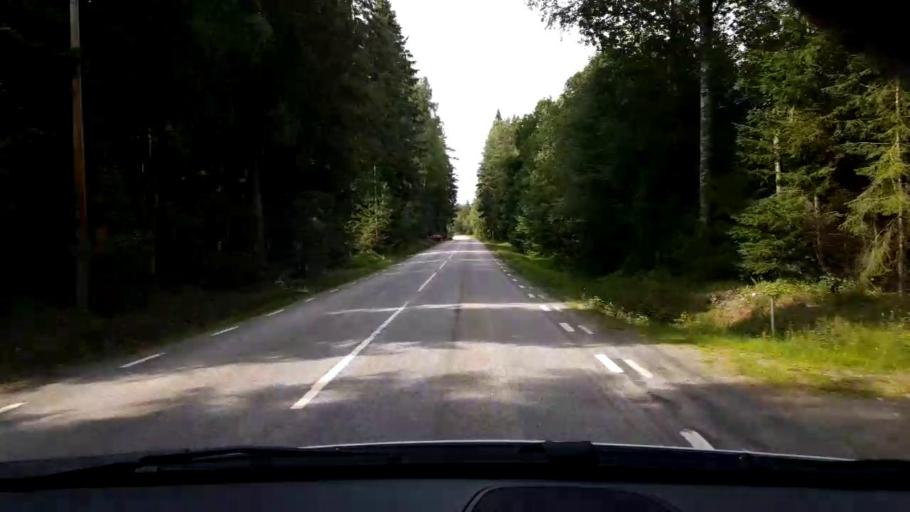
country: SE
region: Joenkoeping
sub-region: Vetlanda Kommun
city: Vetlanda
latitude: 57.3583
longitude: 15.0708
